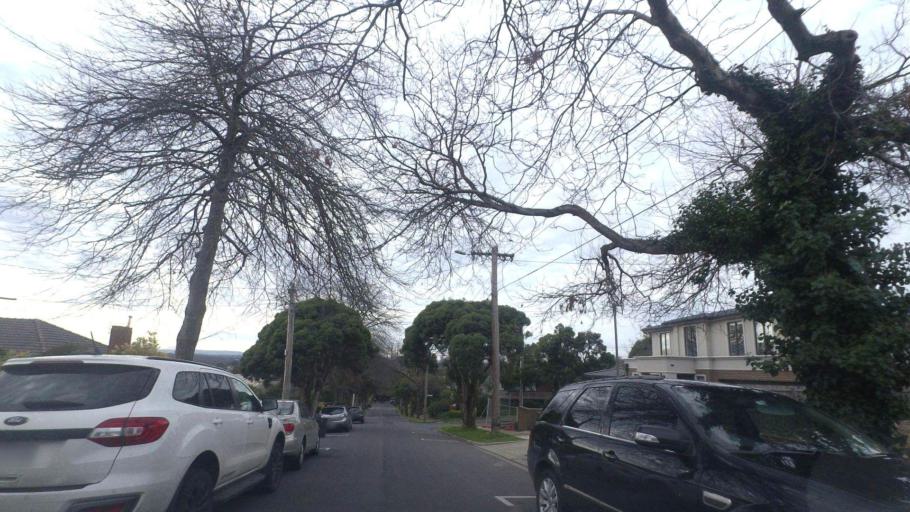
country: AU
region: Victoria
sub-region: Manningham
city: Templestowe Lower
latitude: -37.7669
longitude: 145.1083
